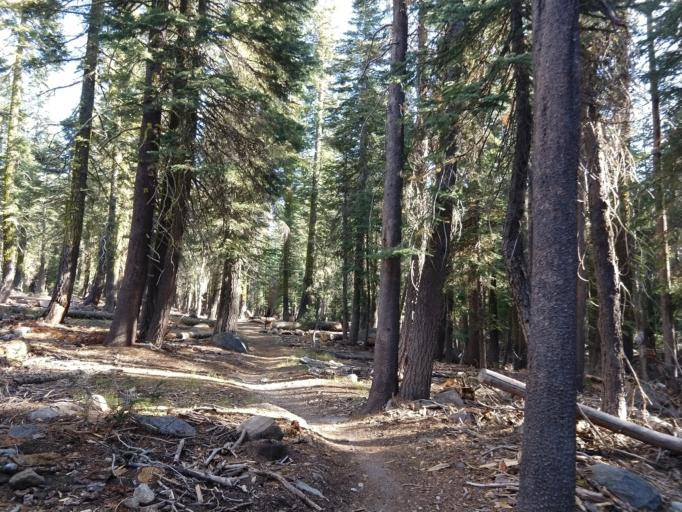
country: US
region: California
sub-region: Plumas County
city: Chester
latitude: 40.4487
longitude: -121.4037
